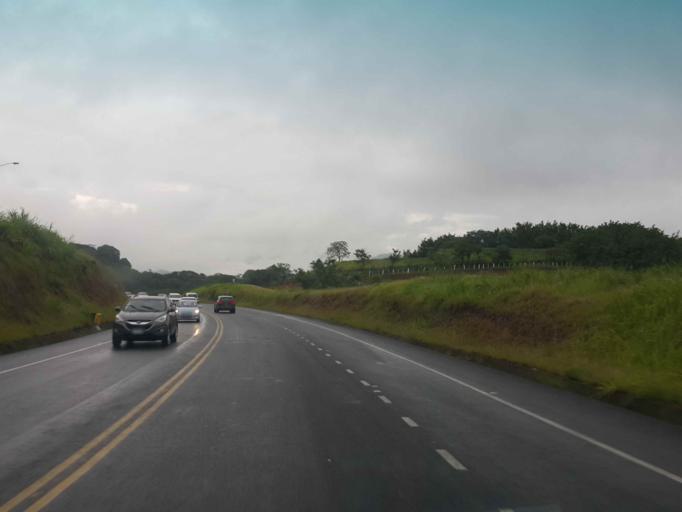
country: CR
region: Heredia
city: Colon
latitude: 9.9430
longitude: -84.2286
